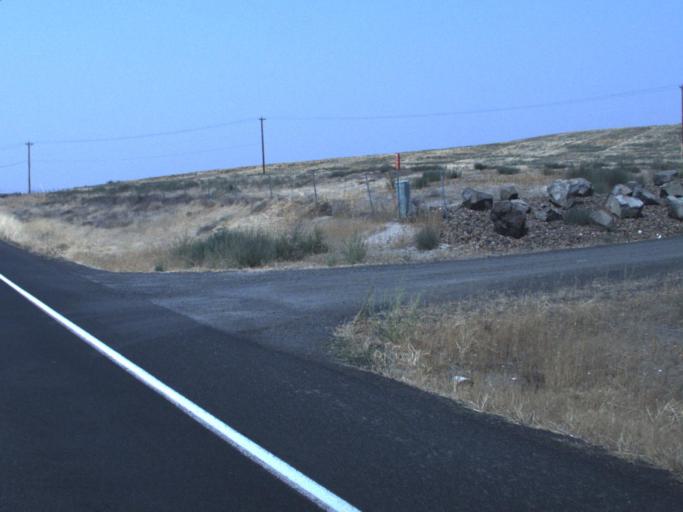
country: US
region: Washington
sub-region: Yakima County
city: Zillah
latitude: 46.5119
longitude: -120.1991
